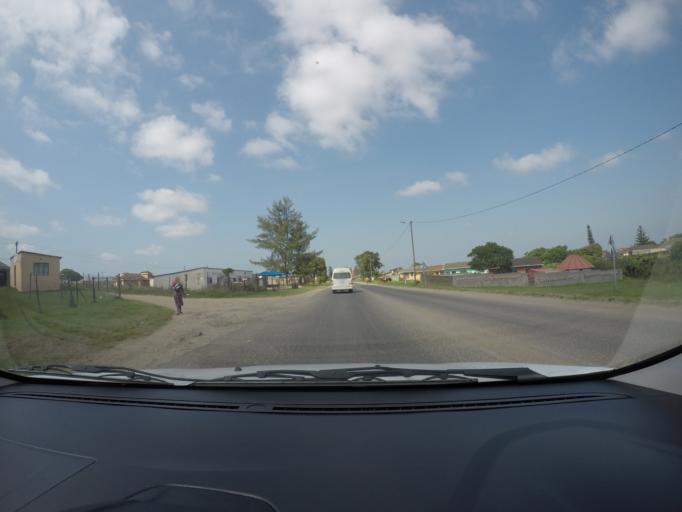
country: ZA
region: KwaZulu-Natal
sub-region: uThungulu District Municipality
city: eSikhawini
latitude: -28.8862
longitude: 31.8991
